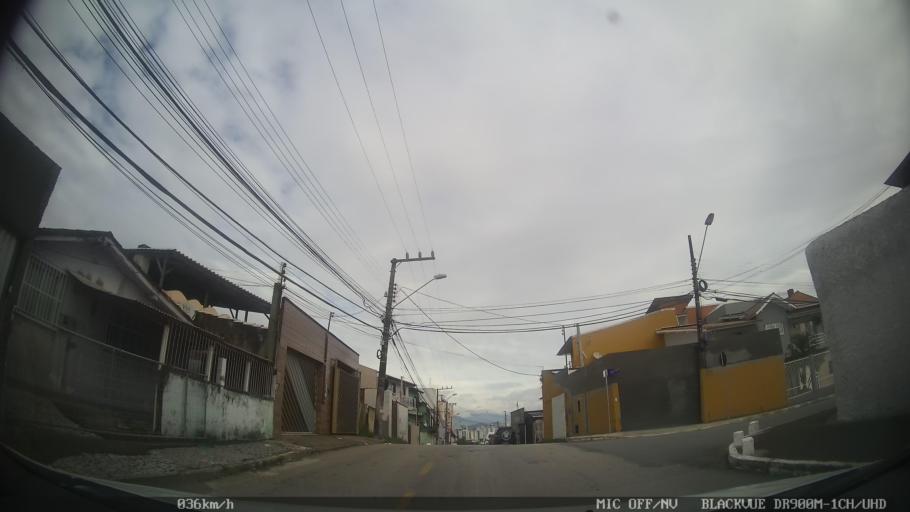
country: BR
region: Santa Catarina
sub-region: Sao Jose
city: Campinas
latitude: -27.5845
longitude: -48.6078
